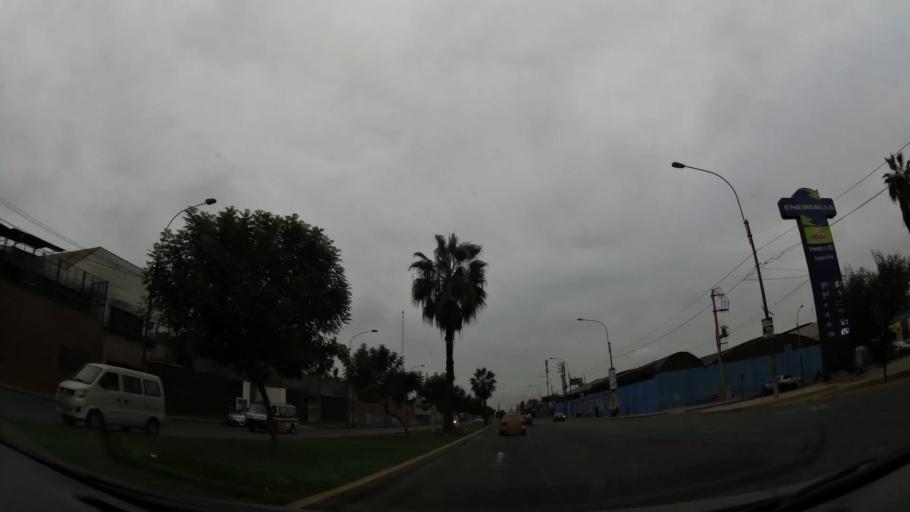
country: PE
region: Lima
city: Lima
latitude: -12.0567
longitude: -77.0624
